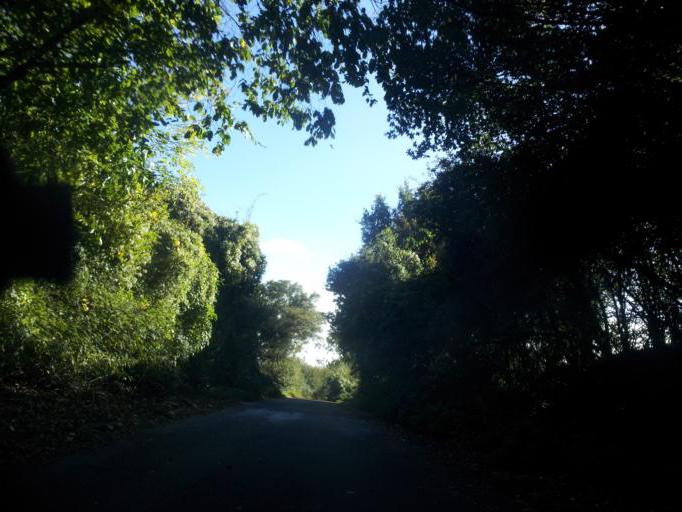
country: GB
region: England
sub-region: Kent
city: Newington
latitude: 51.3382
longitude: 0.6383
